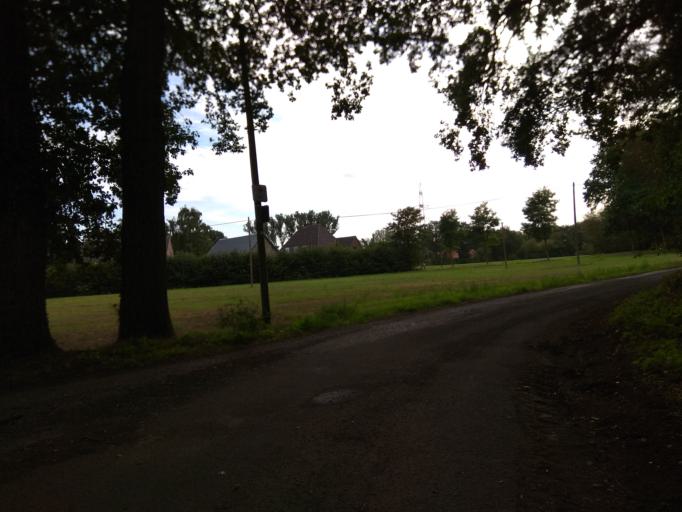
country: DE
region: North Rhine-Westphalia
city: Marl
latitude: 51.7034
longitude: 7.0613
